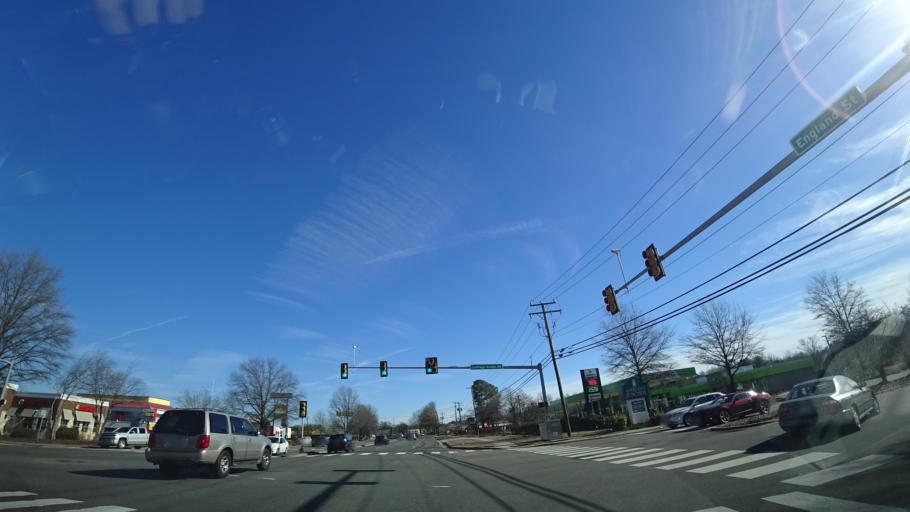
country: US
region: Virginia
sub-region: Hanover County
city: Ashland
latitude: 37.7582
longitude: -77.4683
